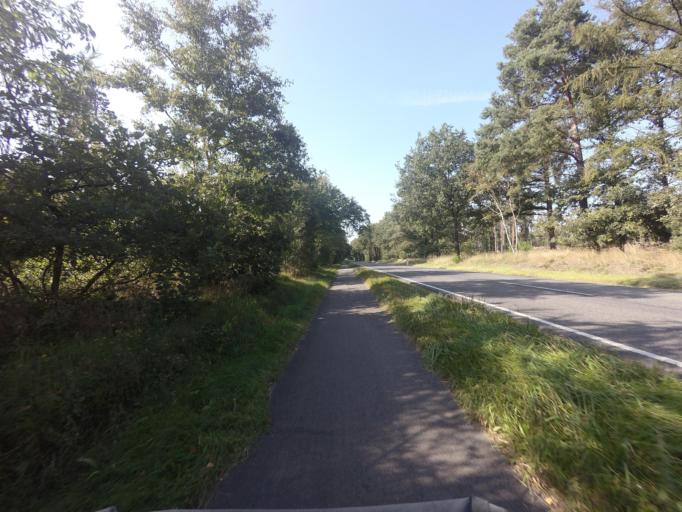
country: DE
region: Lower Saxony
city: Wielen
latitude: 52.5388
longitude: 6.7034
